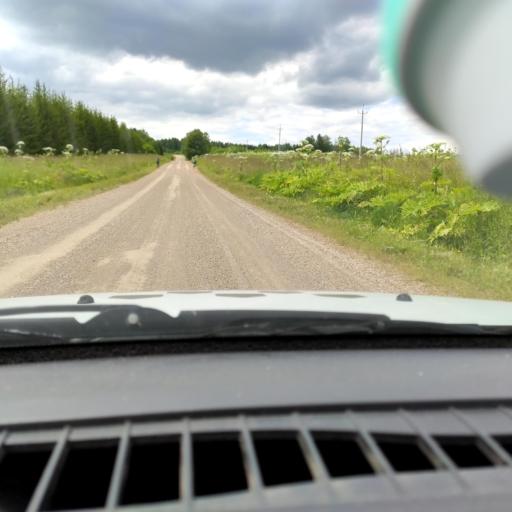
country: RU
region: Perm
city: Suksun
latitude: 57.2136
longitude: 57.6895
